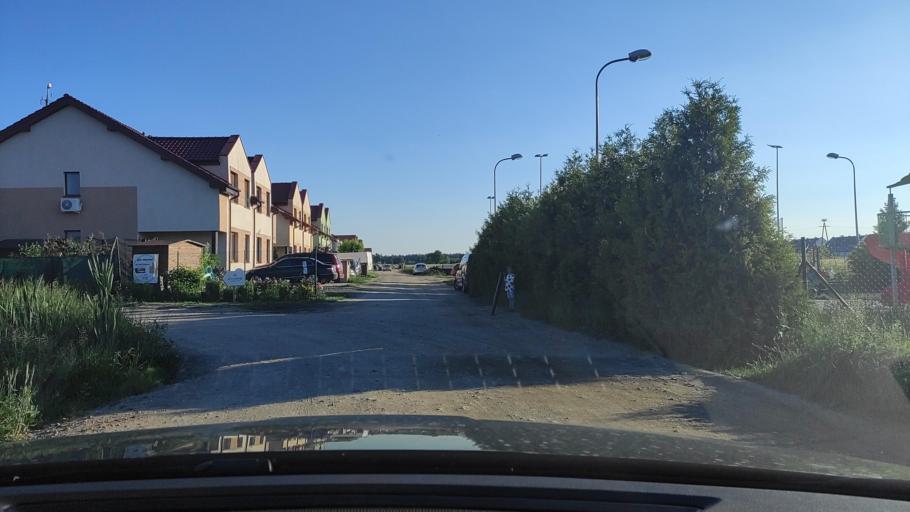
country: PL
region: Greater Poland Voivodeship
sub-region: Powiat poznanski
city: Kornik
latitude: 52.3006
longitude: 17.0872
